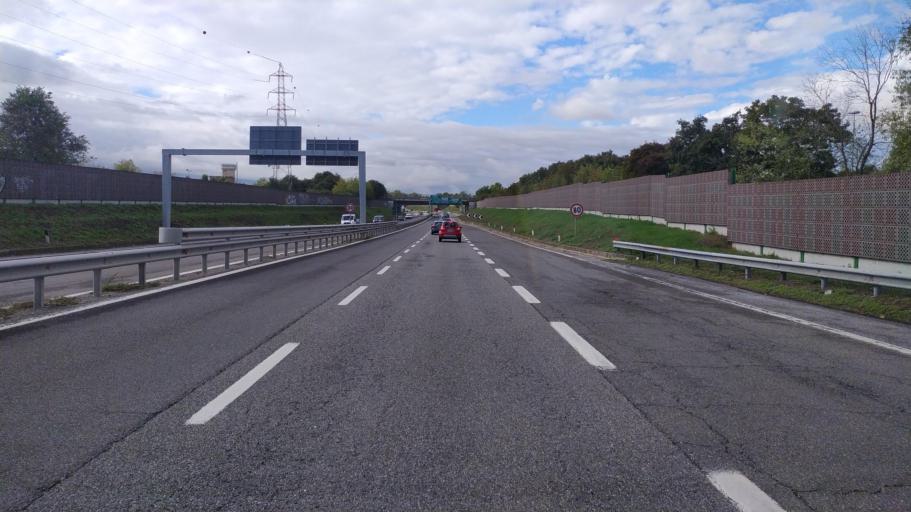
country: IT
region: Lombardy
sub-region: Provincia di Pavia
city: Pavia
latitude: 45.2038
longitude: 9.1455
